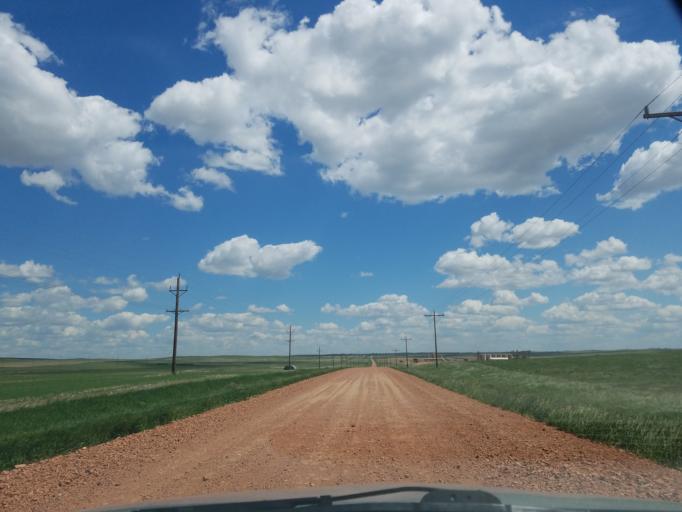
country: US
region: North Dakota
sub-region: McKenzie County
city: Watford City
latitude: 47.8194
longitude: -103.6019
